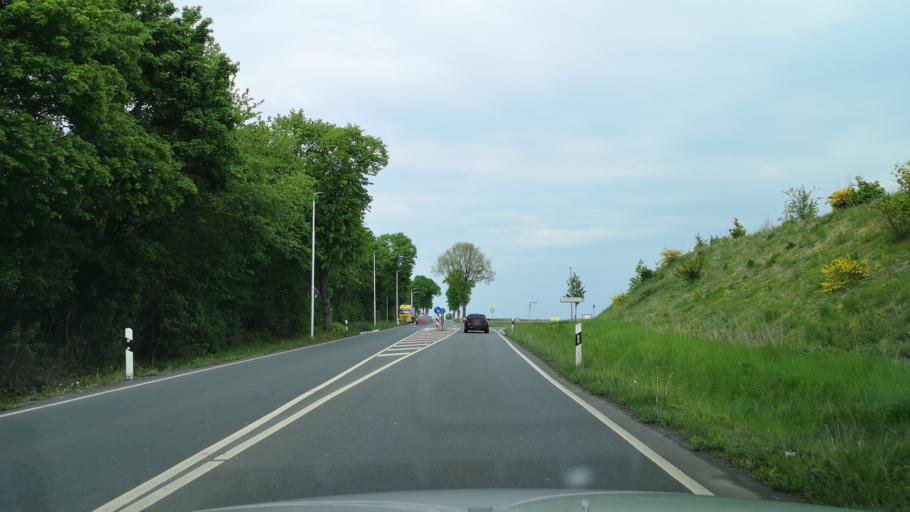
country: DE
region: North Rhine-Westphalia
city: Iserlohn
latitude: 51.4247
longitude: 7.7206
